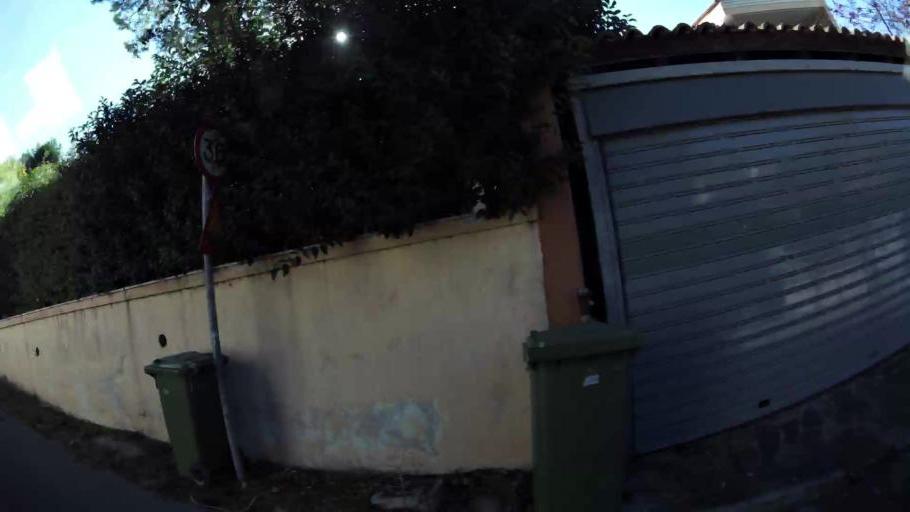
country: GR
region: Attica
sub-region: Nomarchia Anatolikis Attikis
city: Anoixi
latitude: 38.1260
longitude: 23.8592
